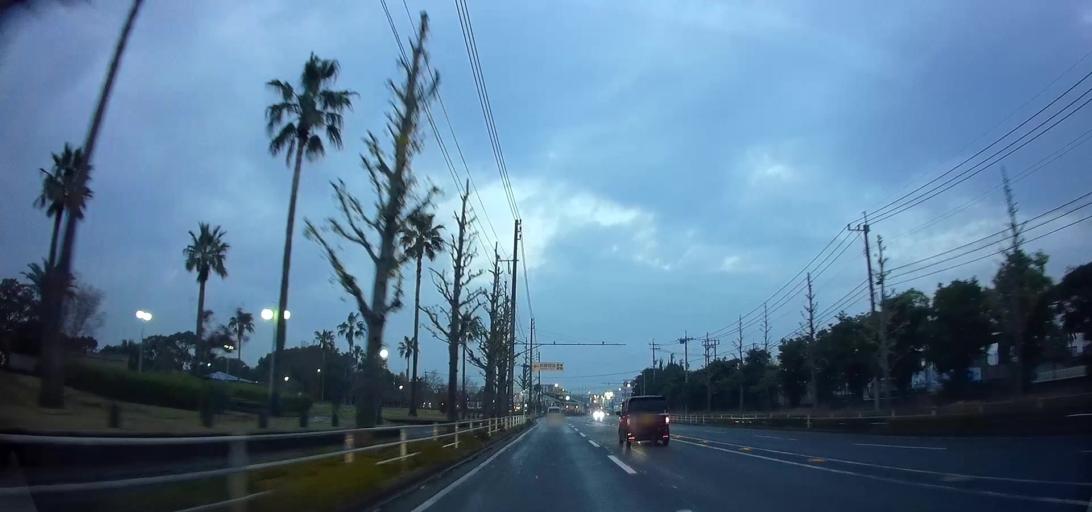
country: JP
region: Nagasaki
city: Omura
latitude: 32.9199
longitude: 129.9400
